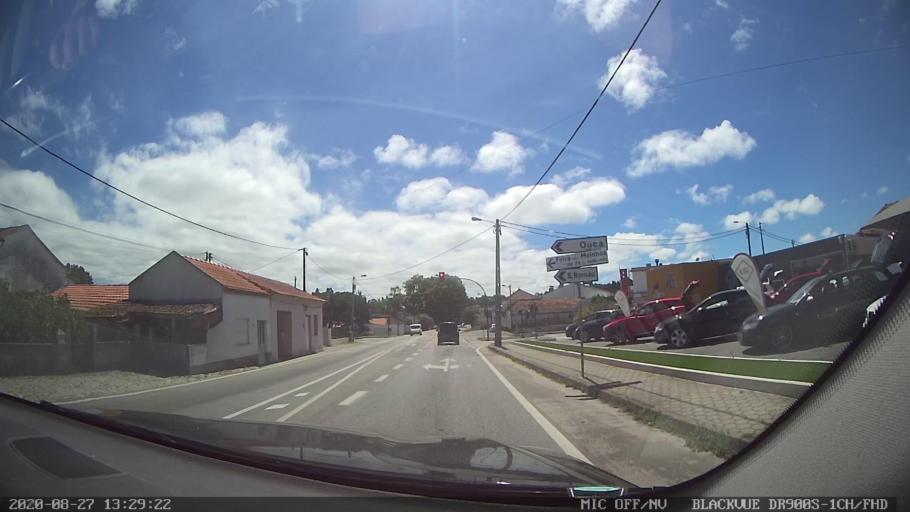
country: PT
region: Aveiro
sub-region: Vagos
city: Vagos
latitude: 40.5117
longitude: -8.6774
